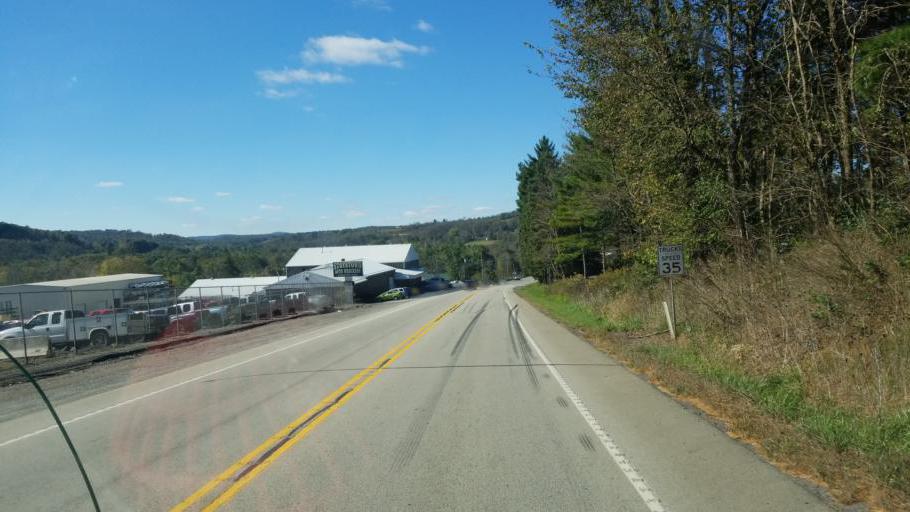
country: US
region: Pennsylvania
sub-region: Somerset County
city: Friedens
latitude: 40.0969
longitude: -78.9388
